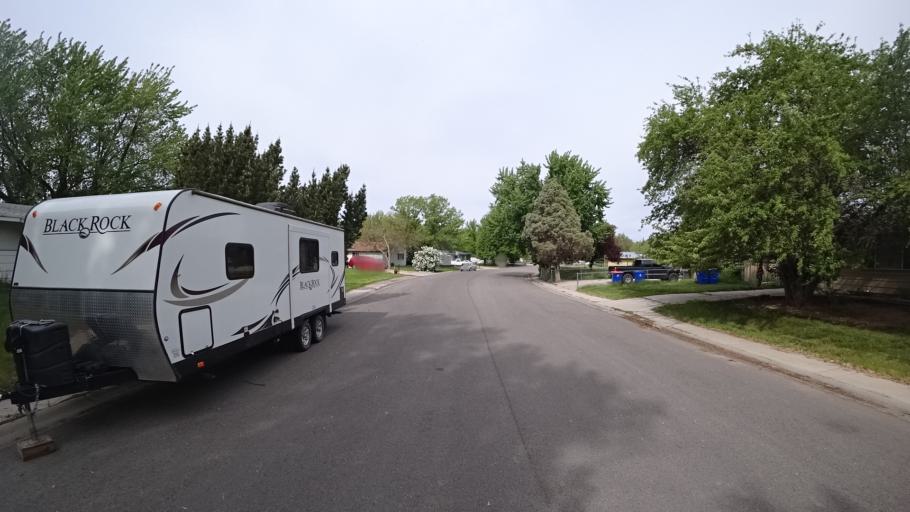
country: US
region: Idaho
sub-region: Ada County
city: Garden City
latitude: 43.5347
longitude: -116.3062
